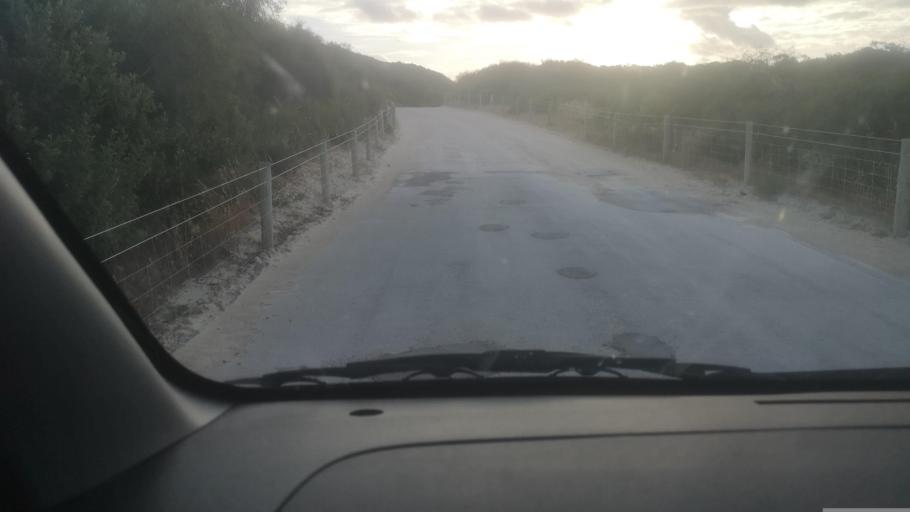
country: AU
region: Western Australia
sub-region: Wanneroo
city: Two Rocks
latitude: -31.5192
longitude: 115.6096
